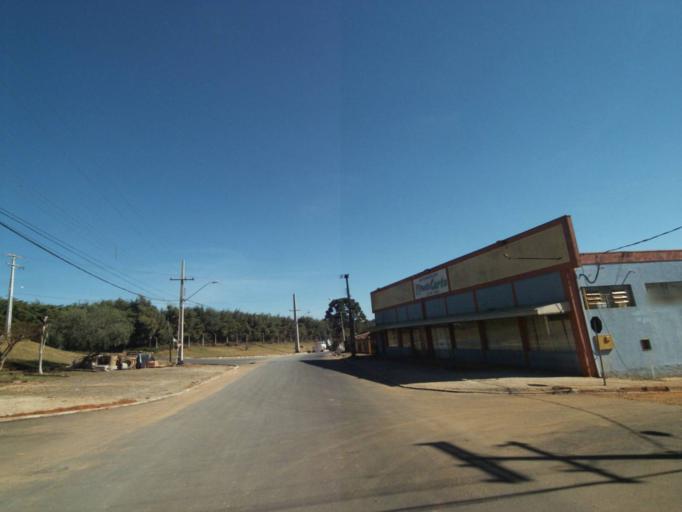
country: BR
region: Parana
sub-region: Tibagi
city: Tibagi
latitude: -24.5211
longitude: -50.4152
